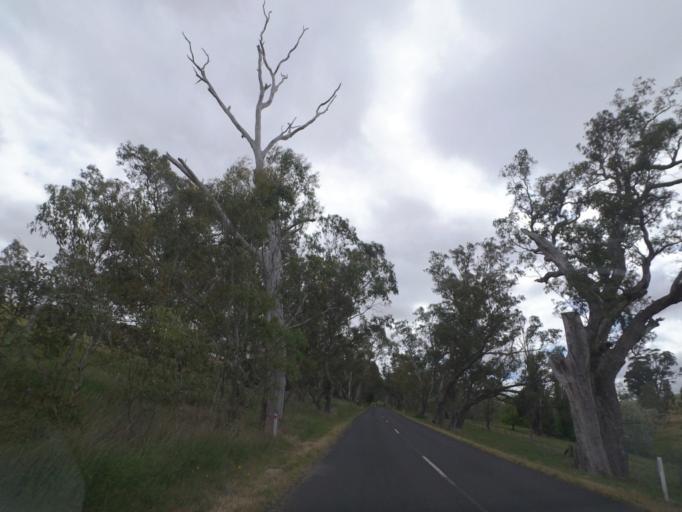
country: AU
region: Victoria
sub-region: Whittlesea
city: Whittlesea
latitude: -37.1965
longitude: 145.0381
